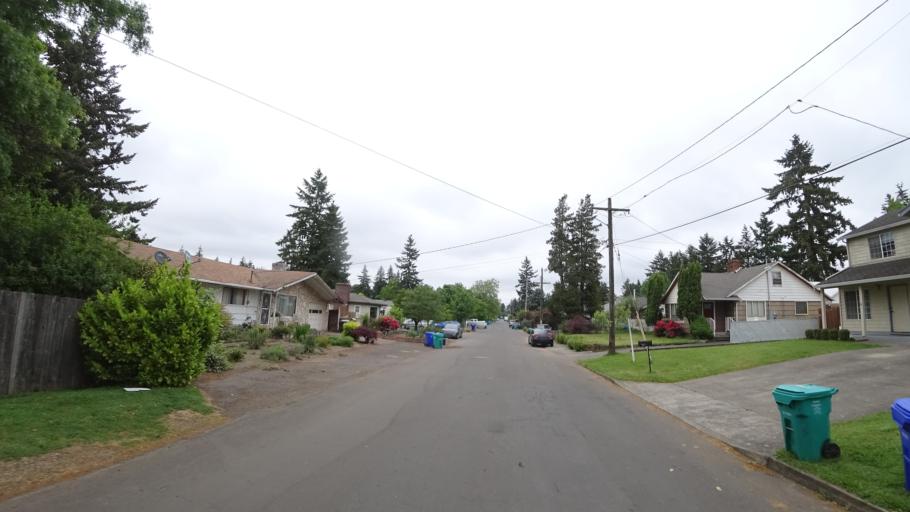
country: US
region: Oregon
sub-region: Multnomah County
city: Portland
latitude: 45.5579
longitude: -122.6092
